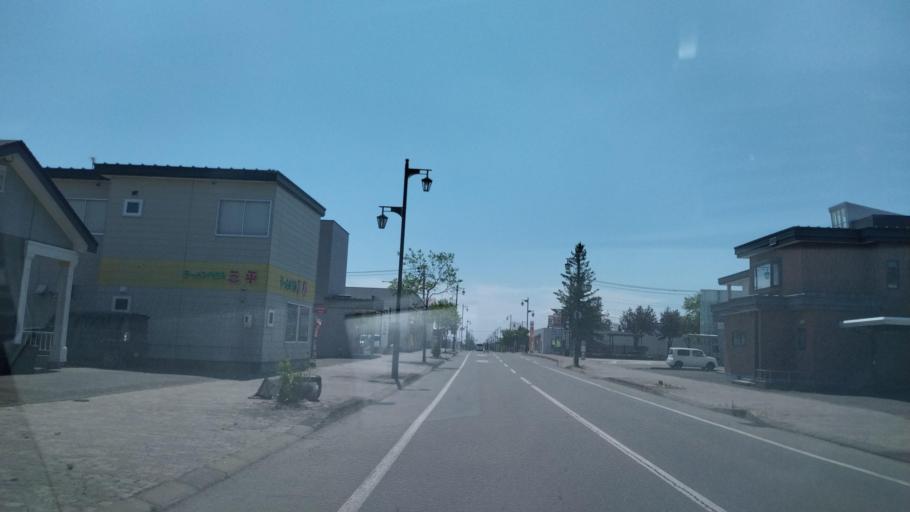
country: JP
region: Hokkaido
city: Otofuke
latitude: 43.1681
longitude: 143.2458
